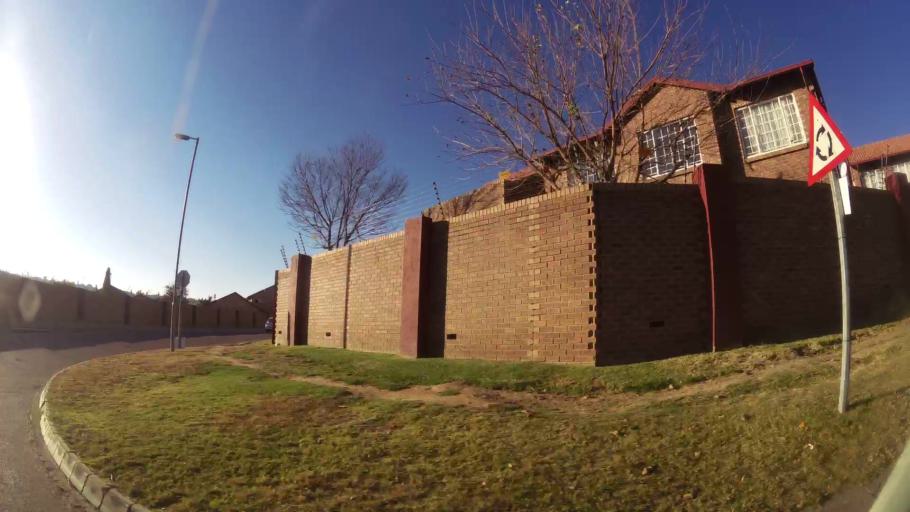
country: ZA
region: Gauteng
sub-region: City of Tshwane Metropolitan Municipality
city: Centurion
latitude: -25.9016
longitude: 28.1439
